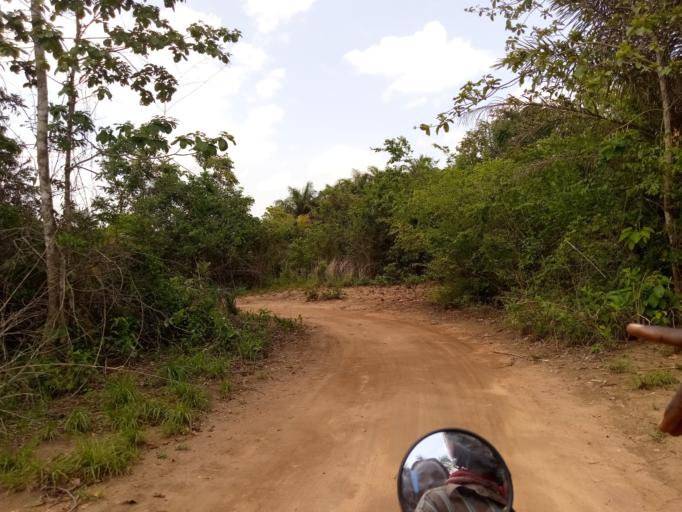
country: SL
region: Western Area
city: Waterloo
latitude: 8.3531
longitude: -13.0040
